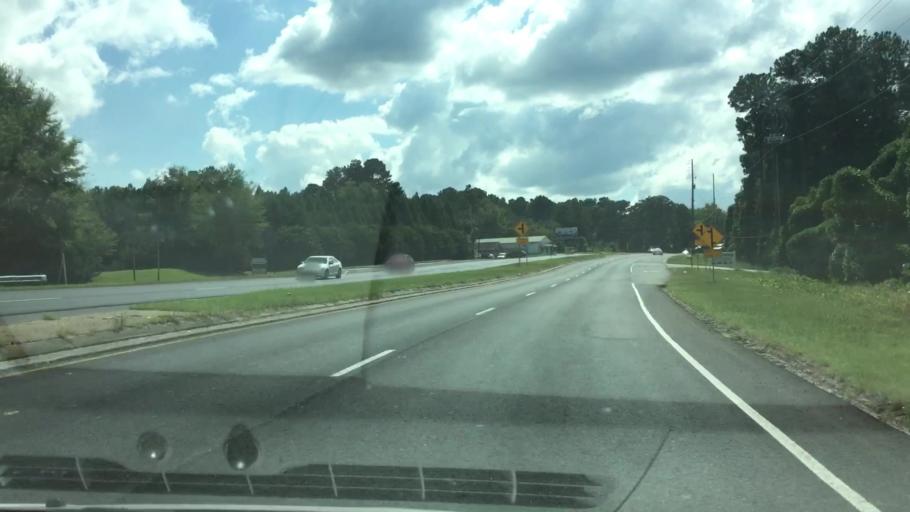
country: US
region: Georgia
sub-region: Fayette County
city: Fayetteville
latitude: 33.4559
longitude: -84.4226
